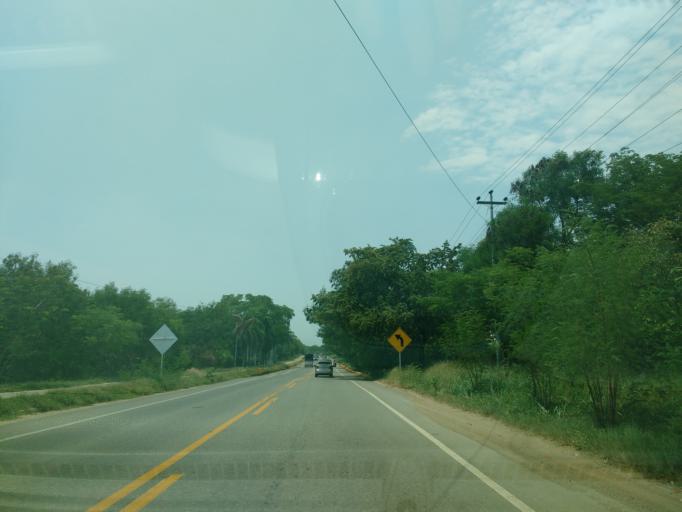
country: CO
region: Cundinamarca
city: Ricaurte
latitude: 4.2596
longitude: -74.7477
